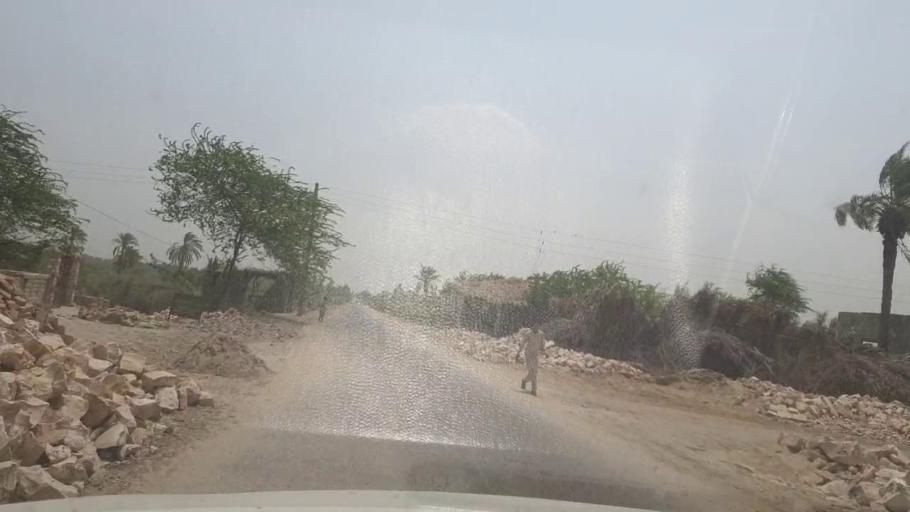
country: PK
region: Sindh
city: Kot Diji
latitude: 27.3753
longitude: 68.7053
